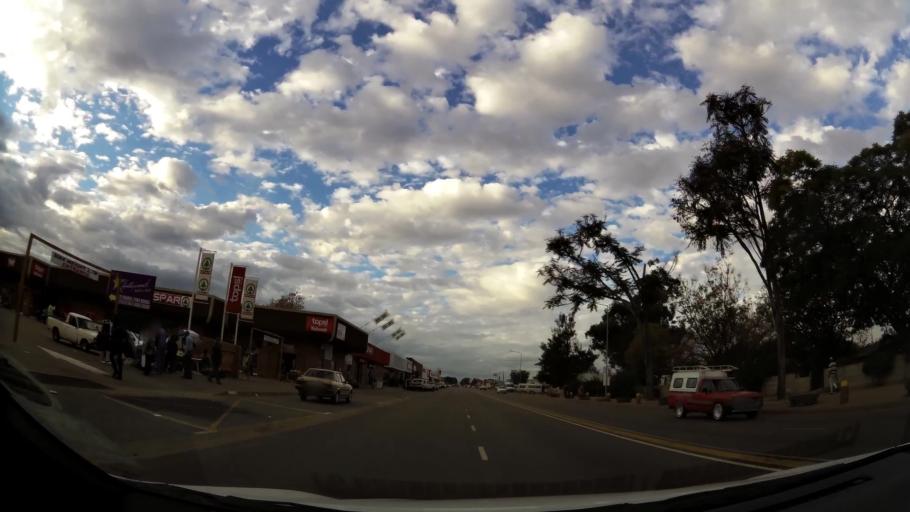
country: ZA
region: Limpopo
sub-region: Waterberg District Municipality
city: Modimolle
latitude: -24.5197
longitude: 28.7141
